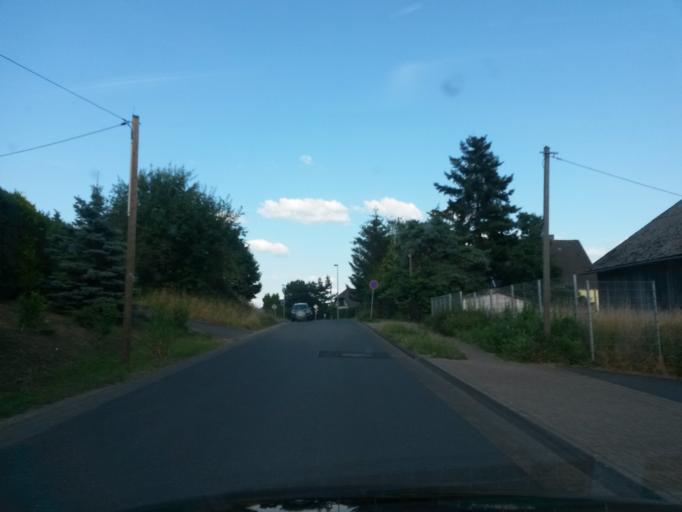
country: DE
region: North Rhine-Westphalia
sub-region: Regierungsbezirk Koln
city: Much
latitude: 50.9002
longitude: 7.3399
